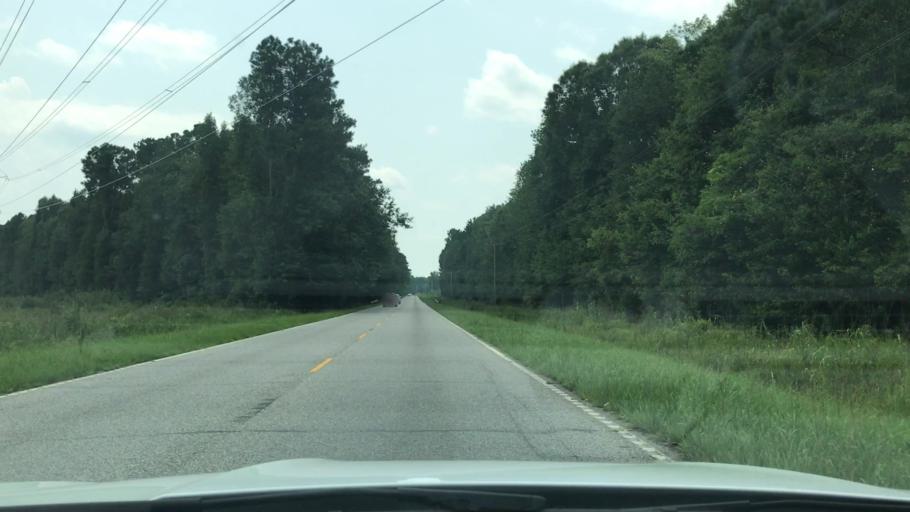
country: US
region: South Carolina
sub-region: Georgetown County
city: Murrells Inlet
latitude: 33.6387
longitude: -79.1807
